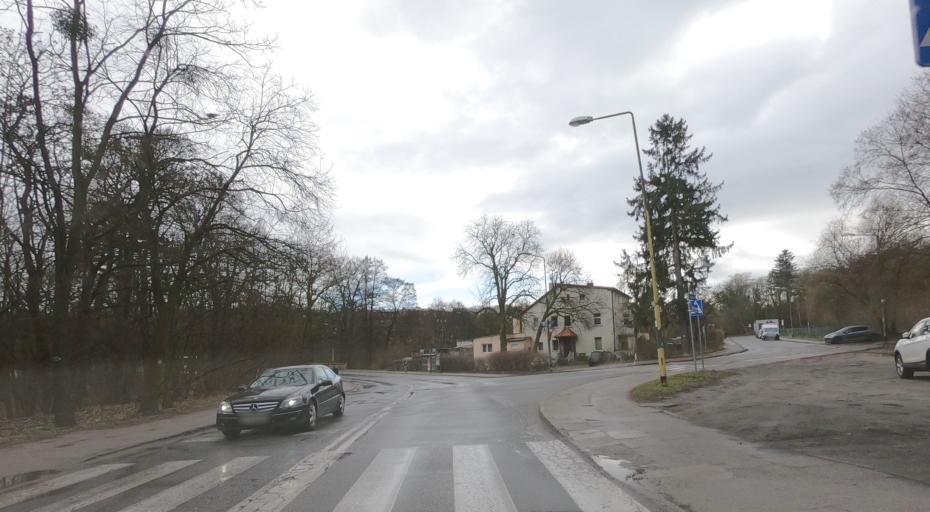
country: PL
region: West Pomeranian Voivodeship
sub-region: Szczecin
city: Szczecin
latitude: 53.3695
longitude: 14.6447
